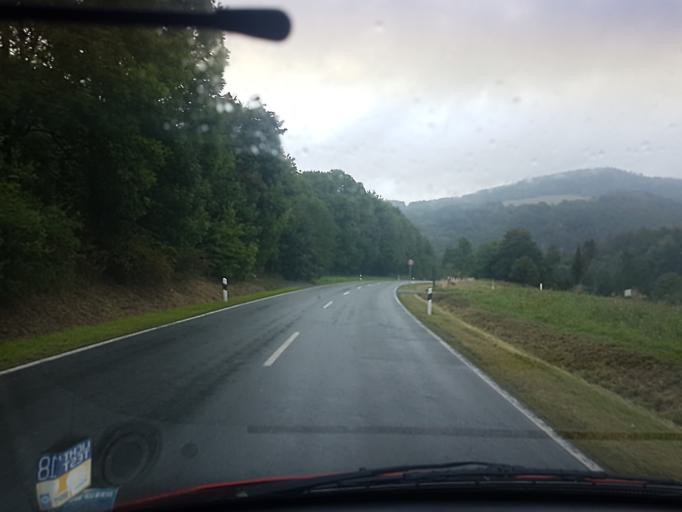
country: DE
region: Bavaria
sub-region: Upper Franconia
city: Goldkronach
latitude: 50.0216
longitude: 11.6904
